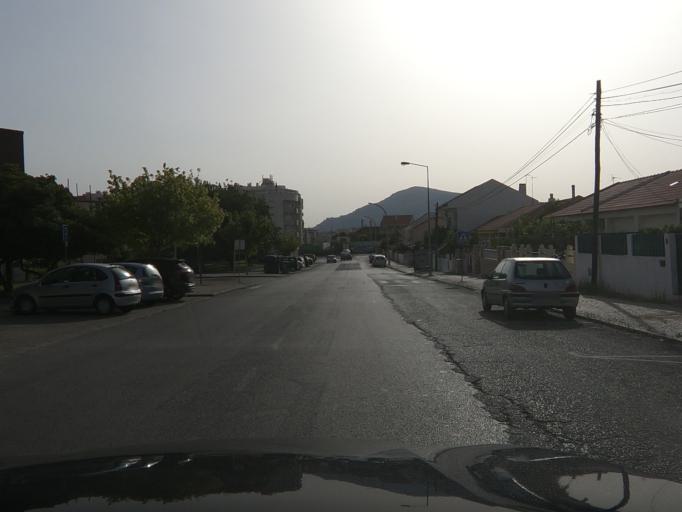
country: PT
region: Setubal
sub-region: Setubal
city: Setubal
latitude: 38.5381
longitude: -8.8806
